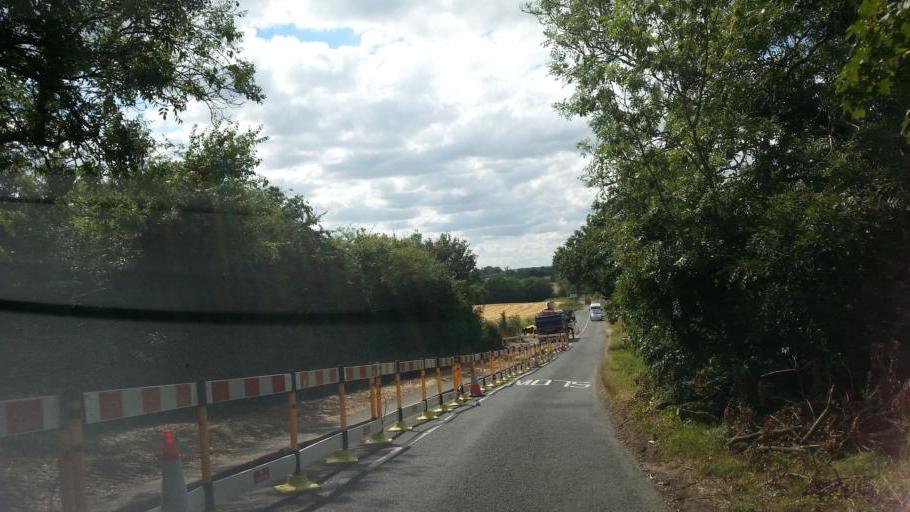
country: GB
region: England
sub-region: Northamptonshire
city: Silverstone
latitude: 52.0934
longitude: -0.9971
